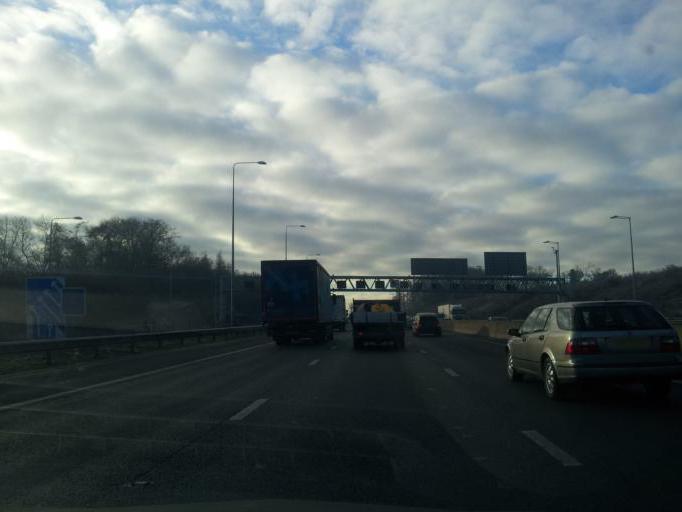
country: GB
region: England
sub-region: Hertfordshire
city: Kings Langley
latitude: 51.6968
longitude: -0.4458
